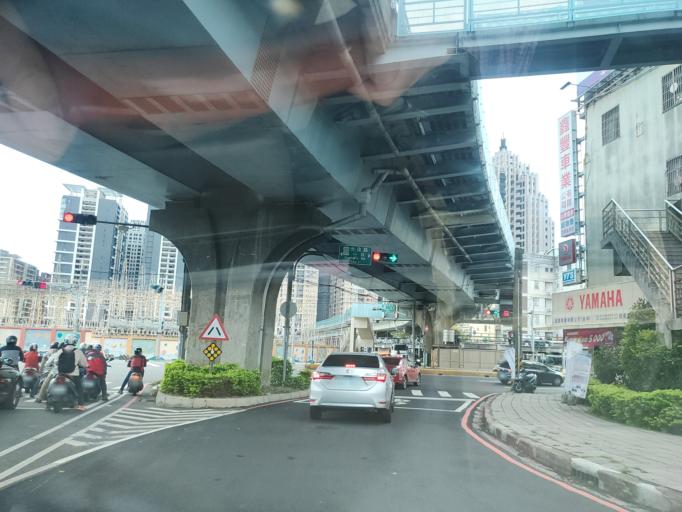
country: TW
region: Taiwan
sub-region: Hsinchu
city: Hsinchu
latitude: 24.7872
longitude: 121.0093
